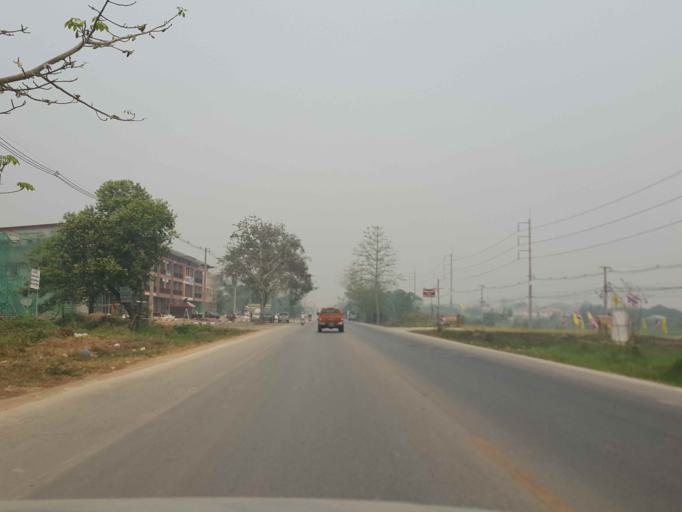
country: TH
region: Chiang Mai
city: San Sai
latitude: 18.8141
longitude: 99.0551
